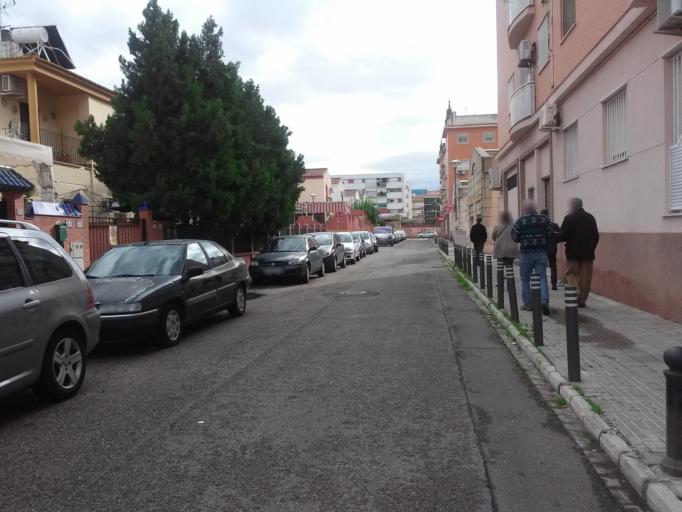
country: ES
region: Andalusia
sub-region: Provincia de Sevilla
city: La Algaba
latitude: 37.4272
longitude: -5.9859
